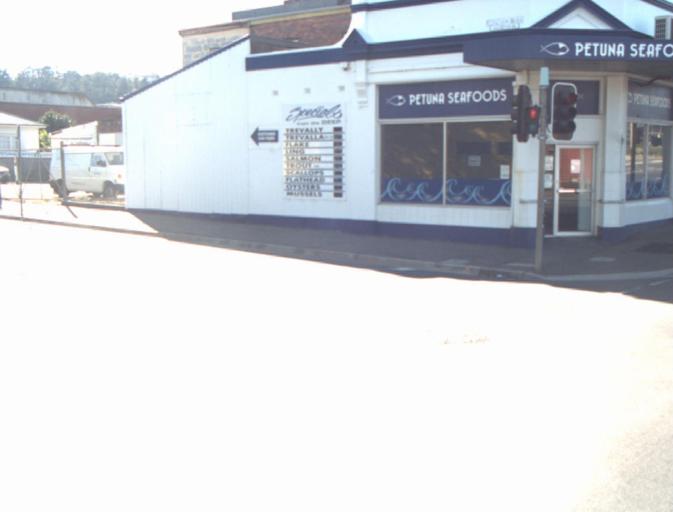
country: AU
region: Tasmania
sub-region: Launceston
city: West Launceston
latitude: -41.4492
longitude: 147.1404
